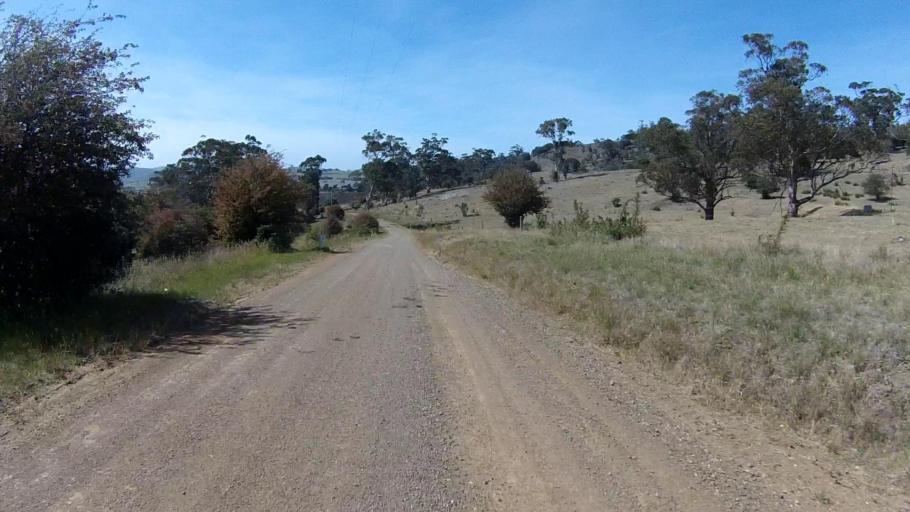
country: AU
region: Tasmania
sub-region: Sorell
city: Sorell
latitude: -42.7426
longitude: 147.6005
